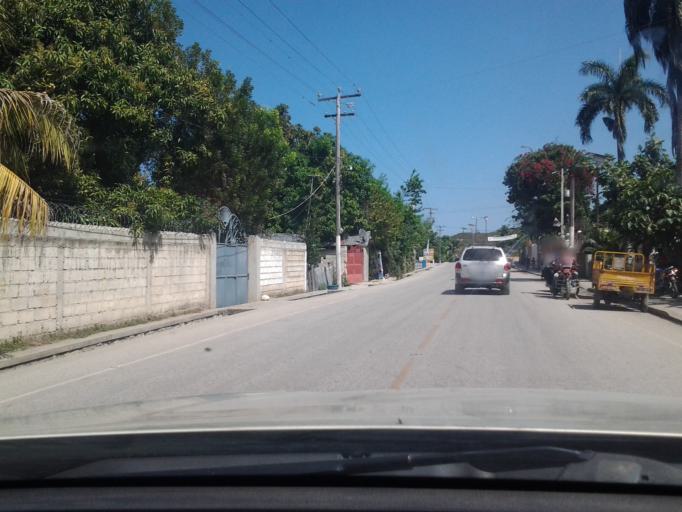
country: HT
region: Ouest
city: Tigwav
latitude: 18.4389
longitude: -72.8517
